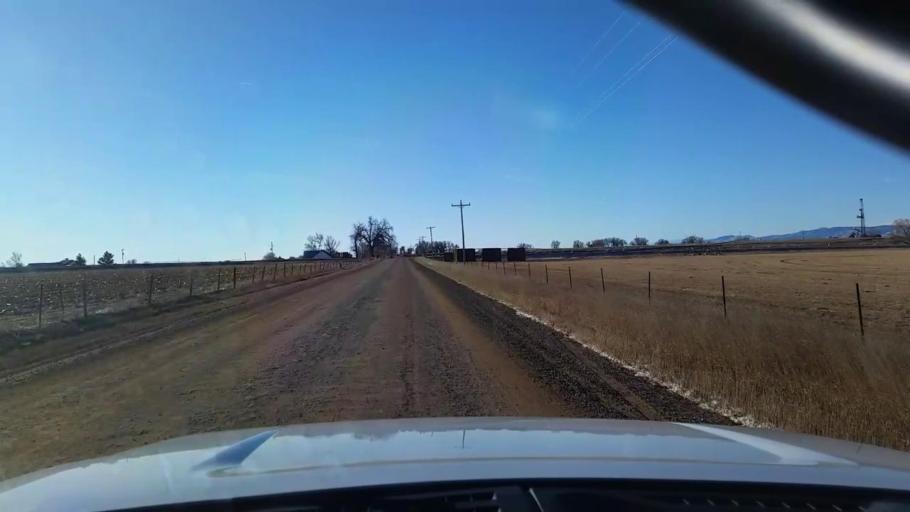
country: US
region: Colorado
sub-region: Larimer County
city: Wellington
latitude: 40.7678
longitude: -105.0382
